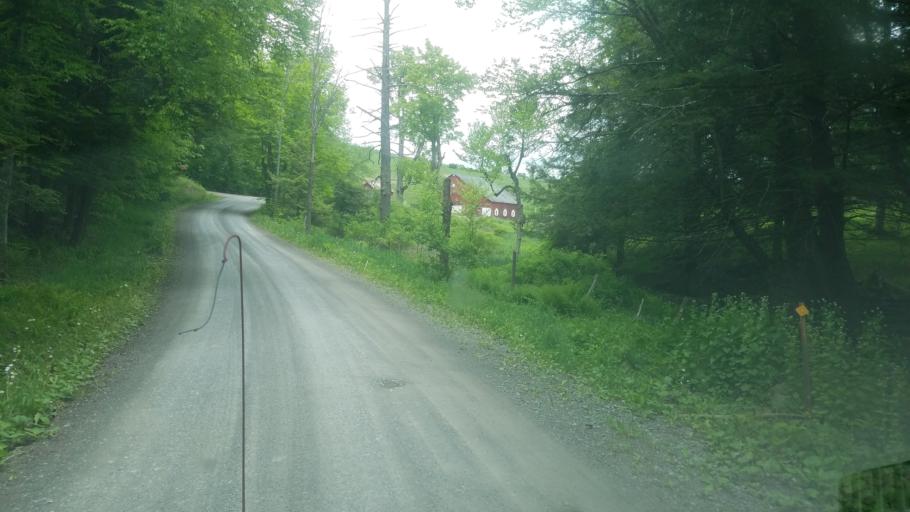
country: US
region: Pennsylvania
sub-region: Tioga County
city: Westfield
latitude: 41.8512
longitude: -77.6036
